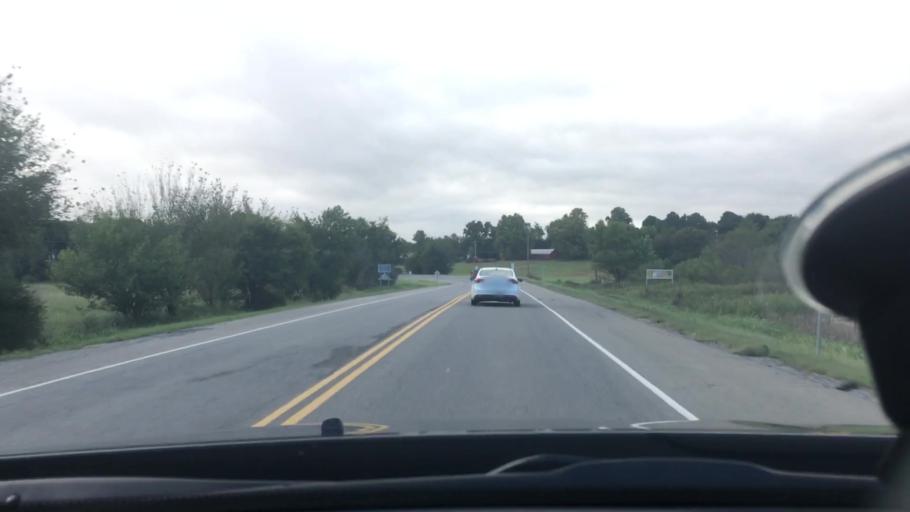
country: US
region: Oklahoma
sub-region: Coal County
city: Coalgate
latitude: 34.5446
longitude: -96.2289
